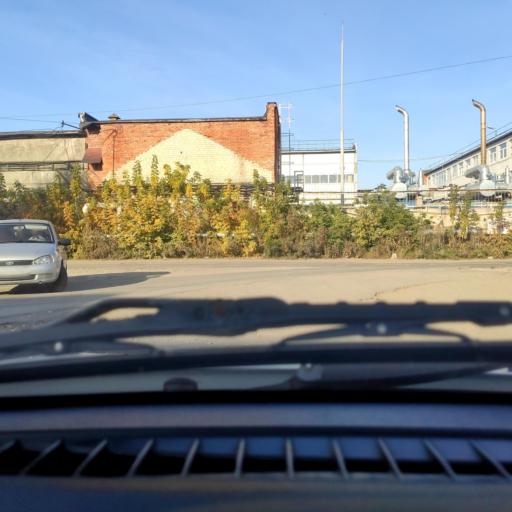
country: RU
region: Samara
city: Tol'yatti
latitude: 53.5327
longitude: 49.4490
